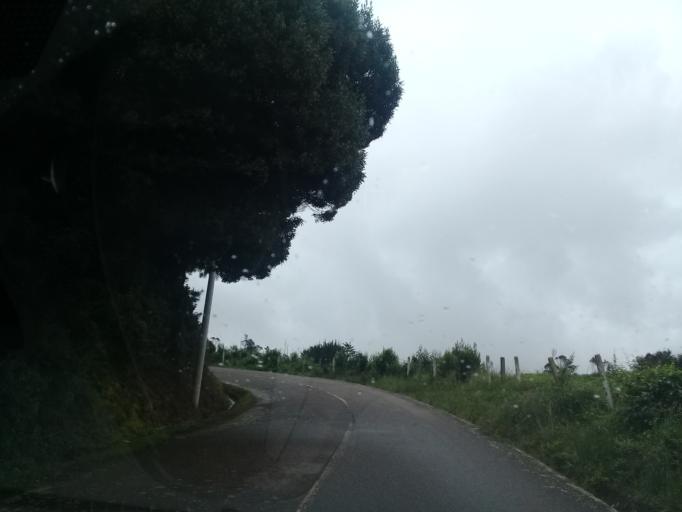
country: CO
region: Boyaca
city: Samaca
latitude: 5.4510
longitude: -73.4281
